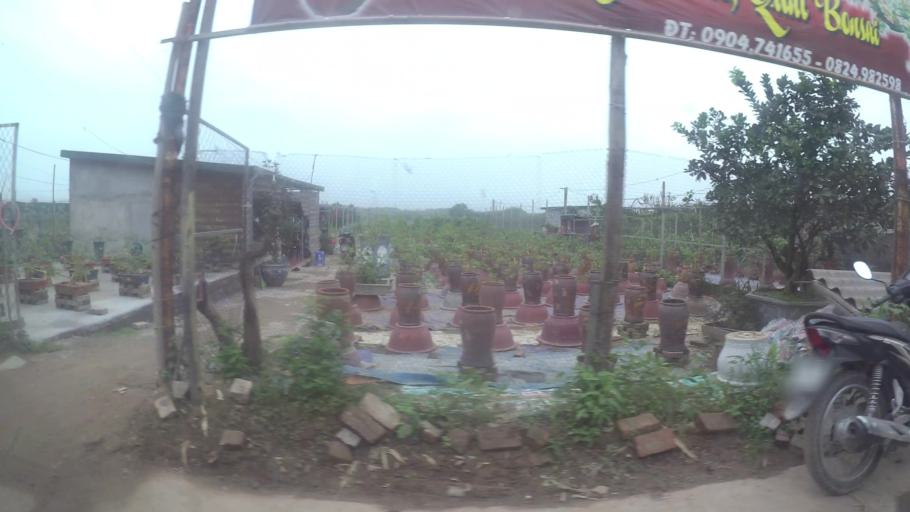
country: VN
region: Ha Noi
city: Tay Ho
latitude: 21.0629
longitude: 105.8380
